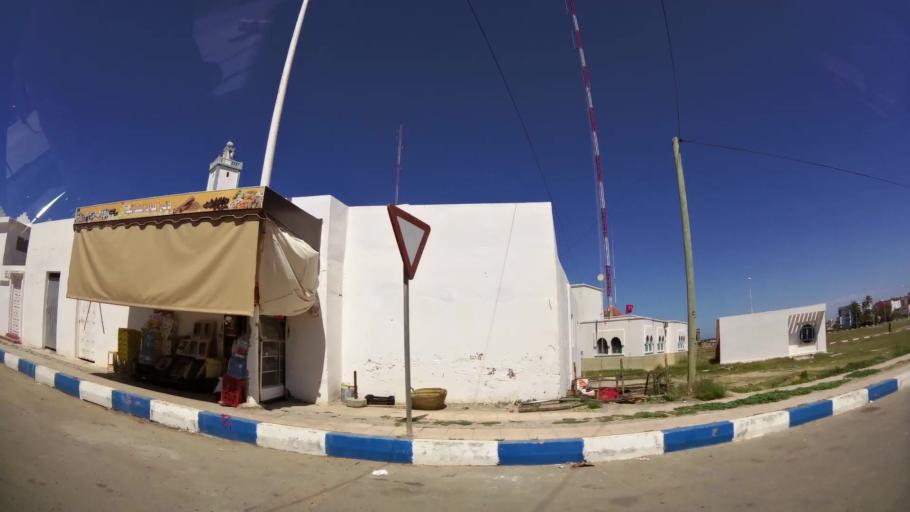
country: MA
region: Oriental
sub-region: Berkane-Taourirt
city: Madagh
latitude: 35.1406
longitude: -2.4238
